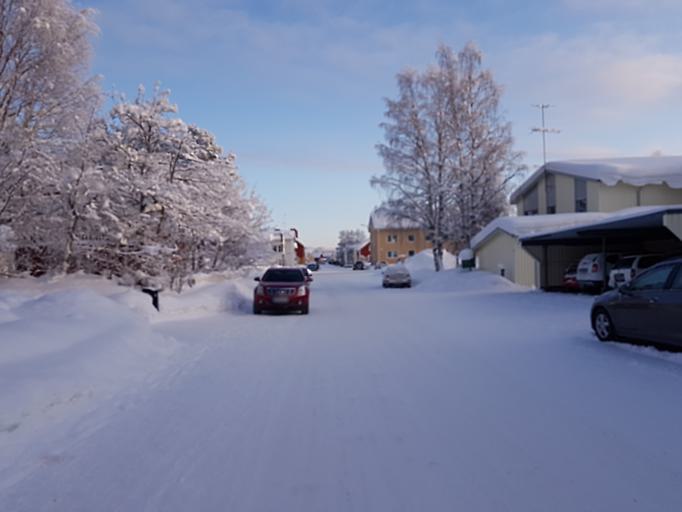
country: SE
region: Norrbotten
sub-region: Jokkmokks Kommun
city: Jokkmokk
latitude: 66.6081
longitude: 19.8226
